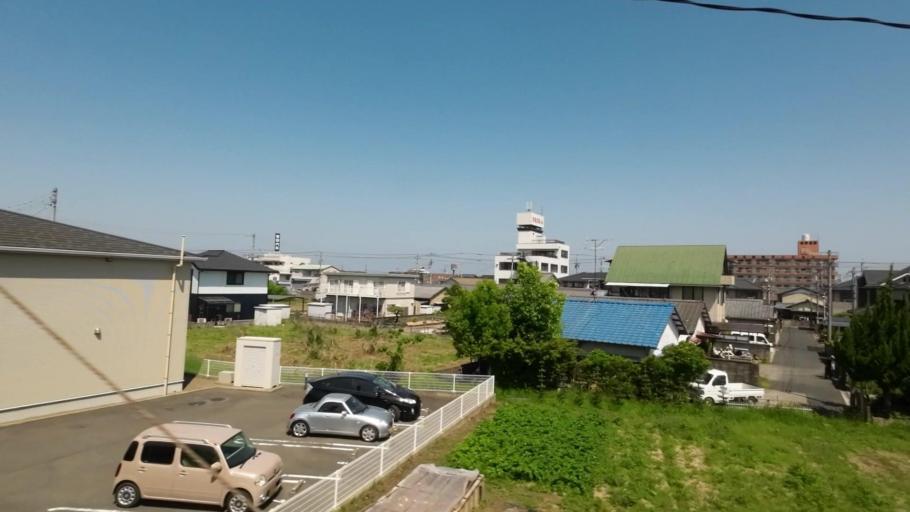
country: JP
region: Ehime
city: Niihama
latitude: 33.9685
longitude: 133.3202
